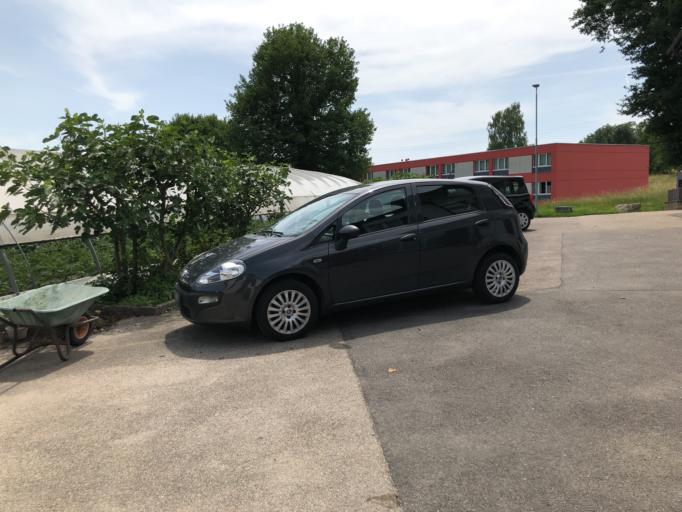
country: CH
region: Neuchatel
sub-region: Neuchatel District
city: Cornaux
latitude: 47.0222
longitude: 7.0291
